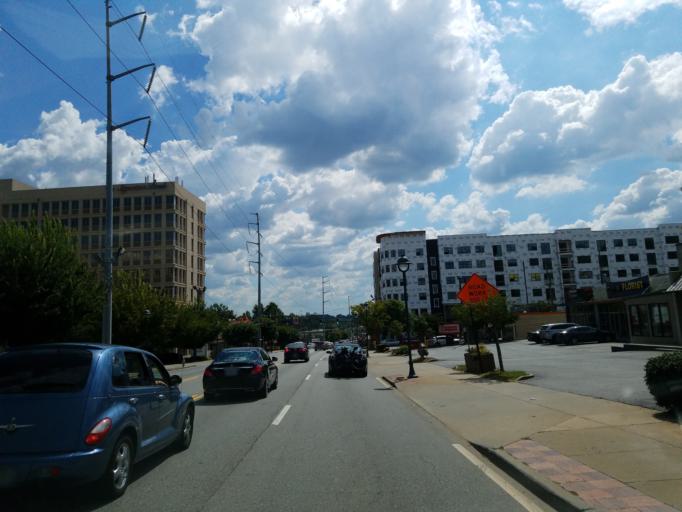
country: US
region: Georgia
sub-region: Fulton County
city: Sandy Springs
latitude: 33.9211
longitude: -84.3792
